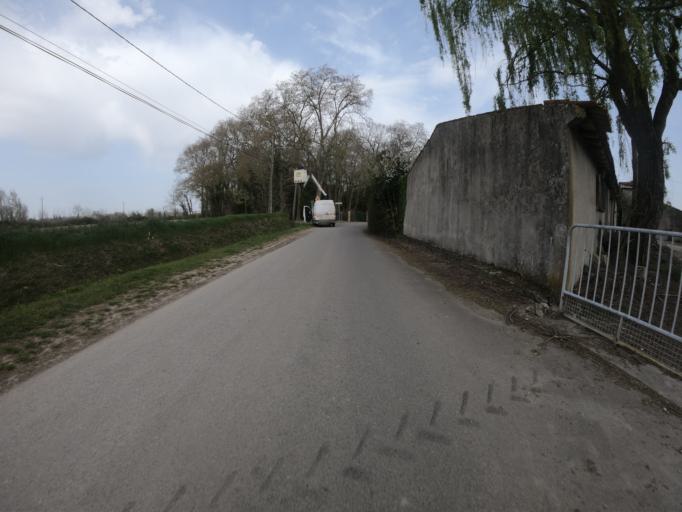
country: FR
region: Languedoc-Roussillon
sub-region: Departement de l'Aude
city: Belpech
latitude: 43.1757
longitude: 1.7292
